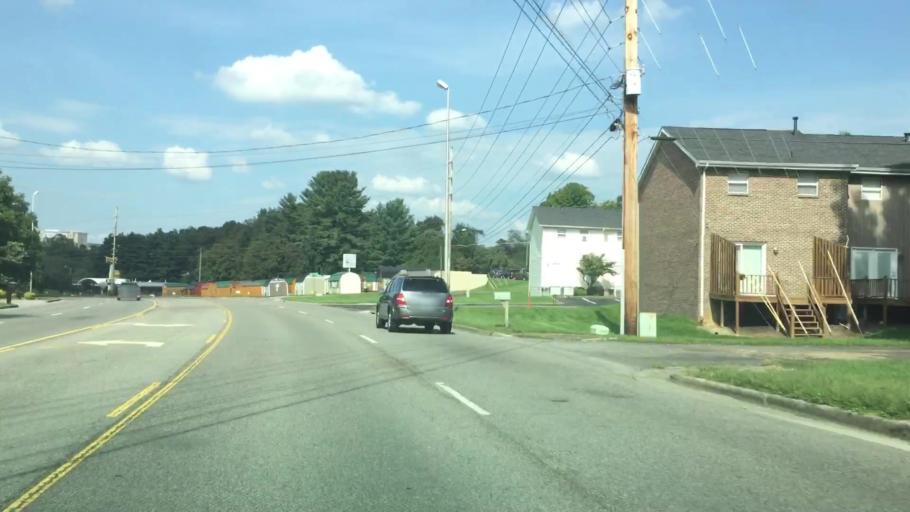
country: US
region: Tennessee
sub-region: Sullivan County
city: Fairmount
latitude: 36.6245
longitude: -82.1233
